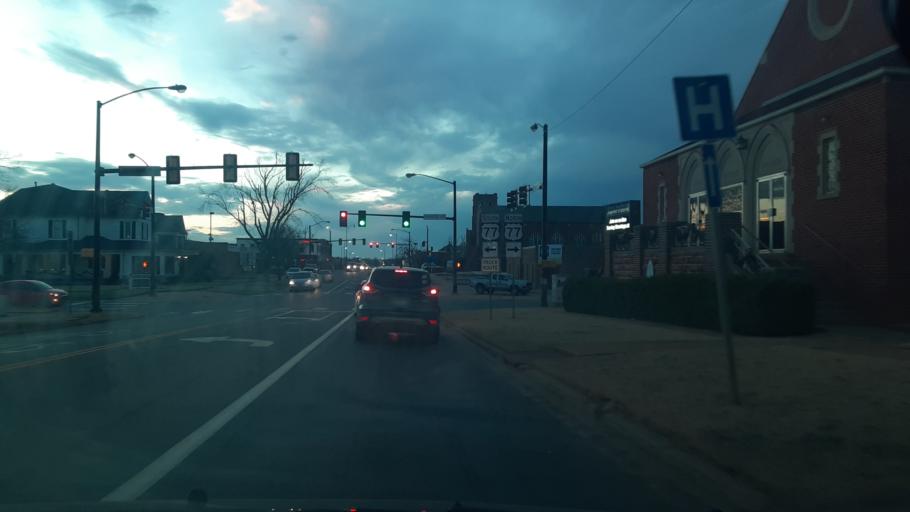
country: US
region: Oklahoma
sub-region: Logan County
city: Guthrie
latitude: 35.8802
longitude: -97.4236
